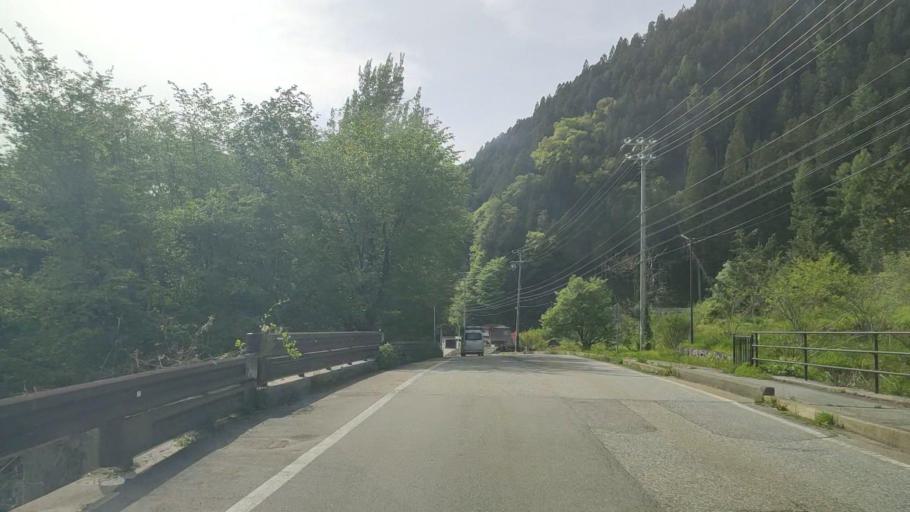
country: JP
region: Gifu
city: Takayama
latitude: 36.2486
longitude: 137.5032
